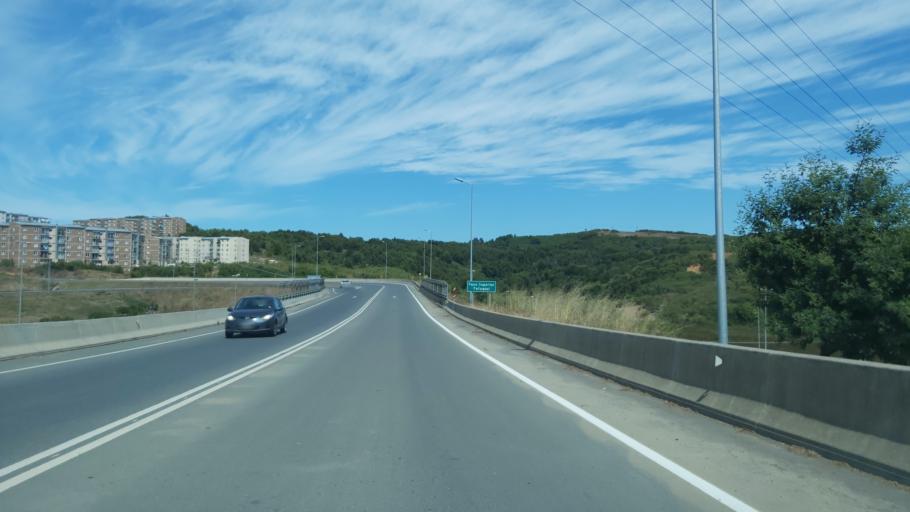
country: CL
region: Biobio
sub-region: Provincia de Concepcion
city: Coronel
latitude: -37.0238
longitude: -73.1344
